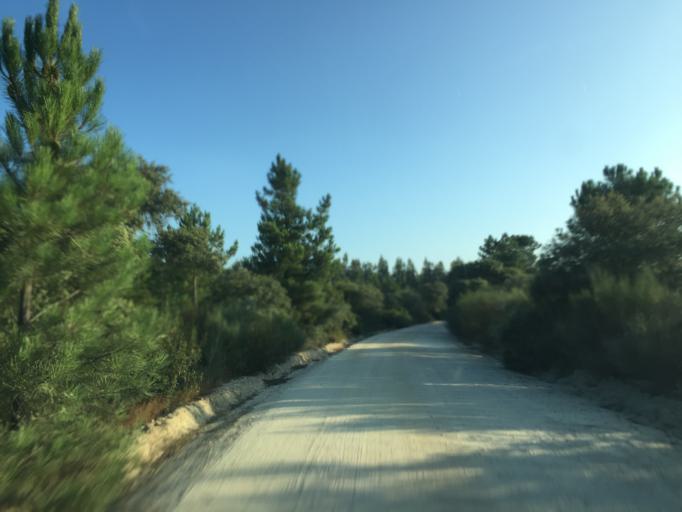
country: PT
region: Portalegre
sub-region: Ponte de Sor
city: Santo Andre
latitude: 39.1550
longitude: -8.3029
